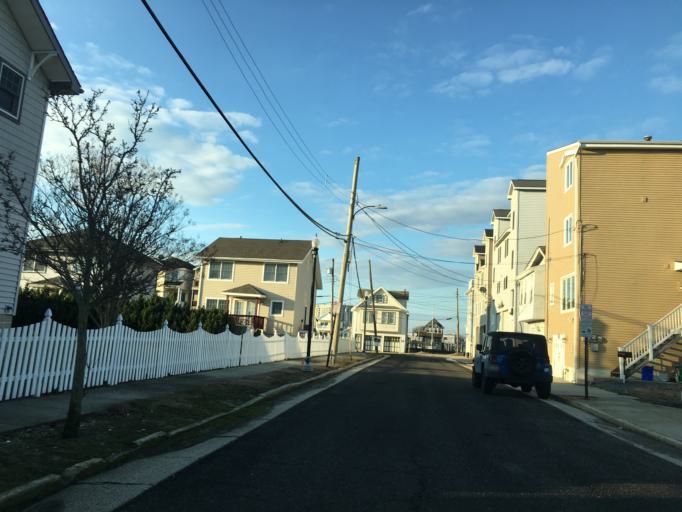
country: US
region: New Jersey
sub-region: Atlantic County
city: Atlantic City
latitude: 39.3750
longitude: -74.4230
